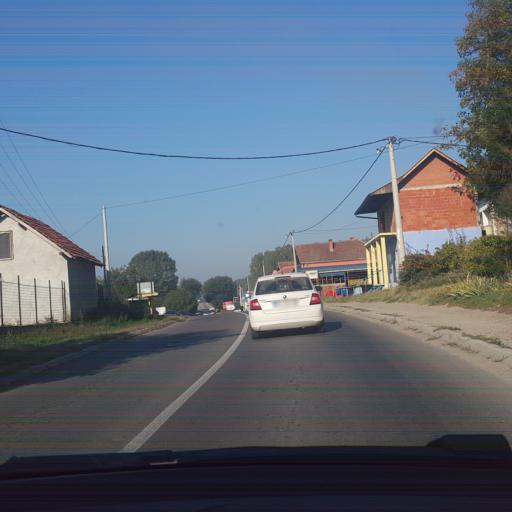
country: RS
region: Central Serbia
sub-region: Toplicki Okrug
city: Prokuplje
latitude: 43.2310
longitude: 21.5615
